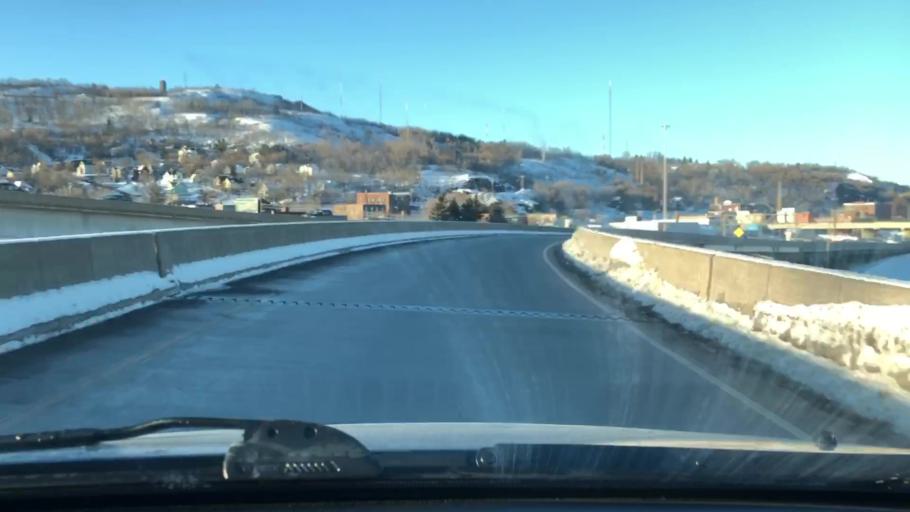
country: US
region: Minnesota
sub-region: Saint Louis County
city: Duluth
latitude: 46.7668
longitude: -92.1203
